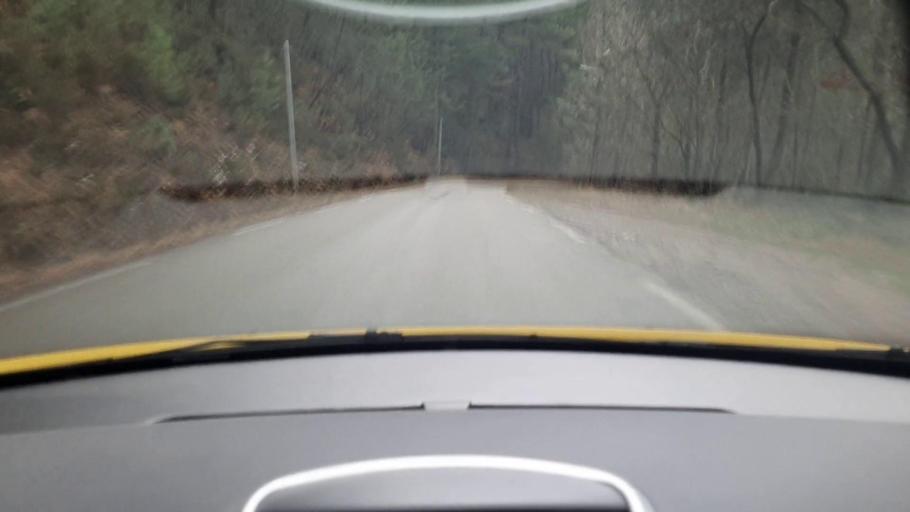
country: FR
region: Languedoc-Roussillon
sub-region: Departement du Gard
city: Besseges
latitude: 44.2755
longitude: 4.0763
